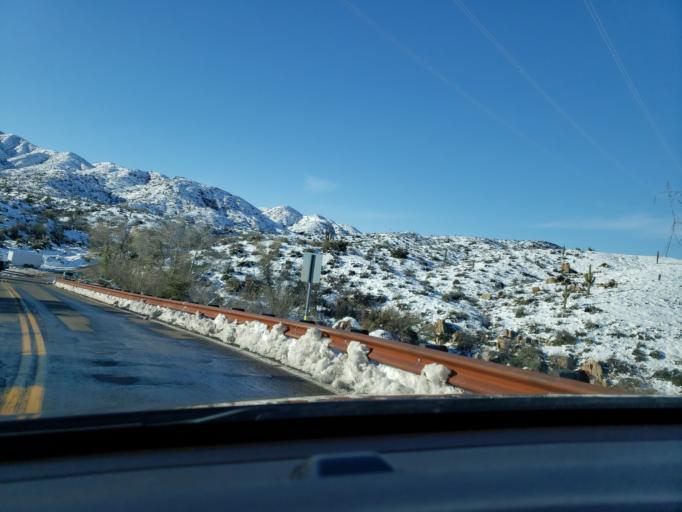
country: US
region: Arizona
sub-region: Maricopa County
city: Carefree
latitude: 33.8778
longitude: -111.8148
